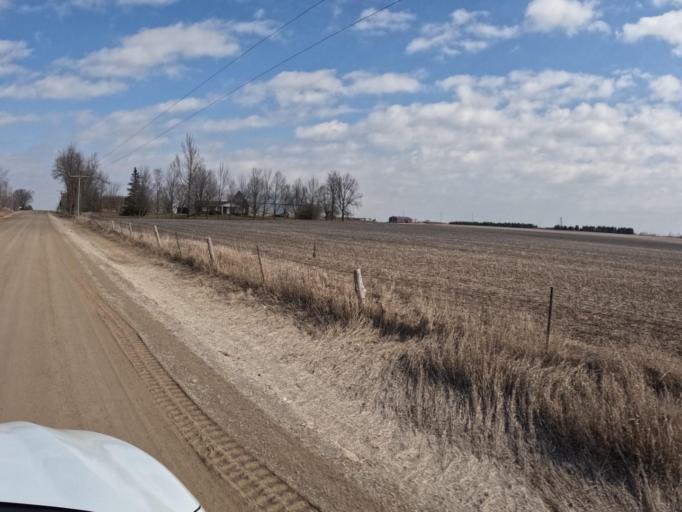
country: CA
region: Ontario
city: Orangeville
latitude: 43.9127
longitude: -80.2537
